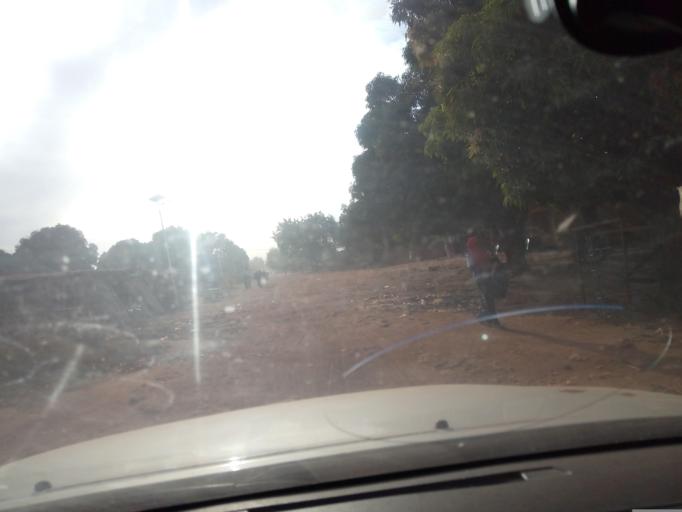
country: ML
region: Sikasso
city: Sikasso
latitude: 11.3158
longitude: -5.6436
